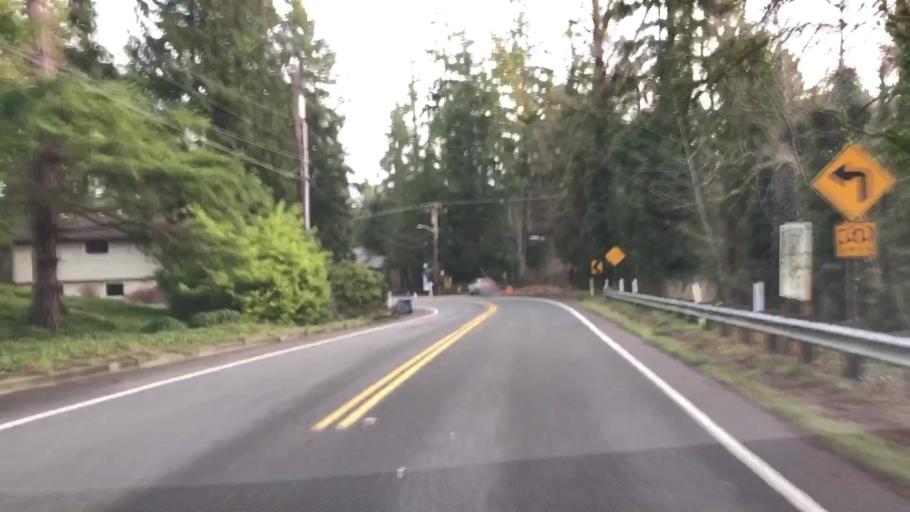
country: US
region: Washington
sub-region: King County
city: Eastgate
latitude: 47.5695
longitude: -122.1232
